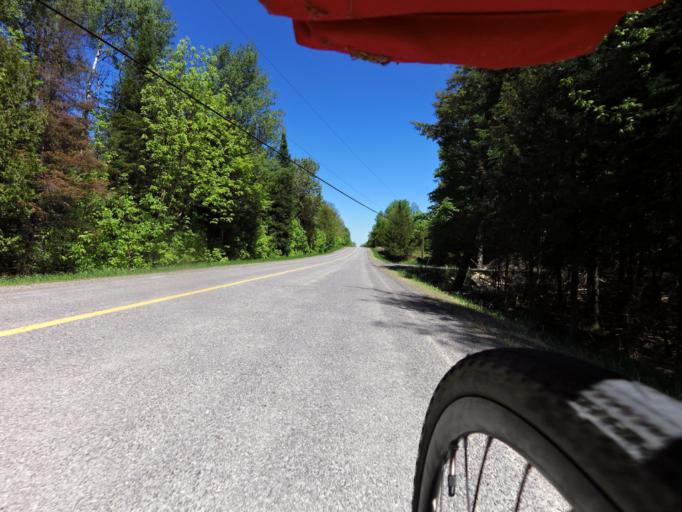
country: CA
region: Ontario
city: Carleton Place
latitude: 45.1656
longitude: -76.4235
